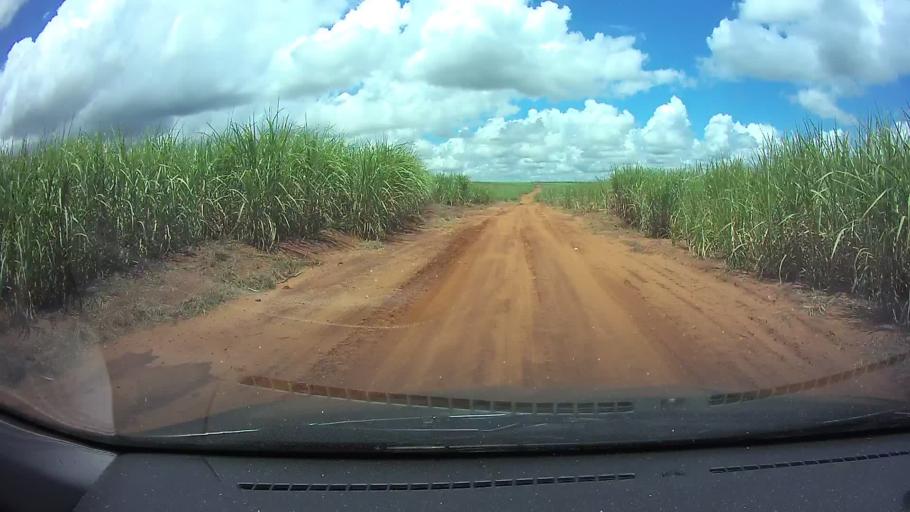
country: PY
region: Paraguari
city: La Colmena
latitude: -25.9550
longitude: -56.7661
